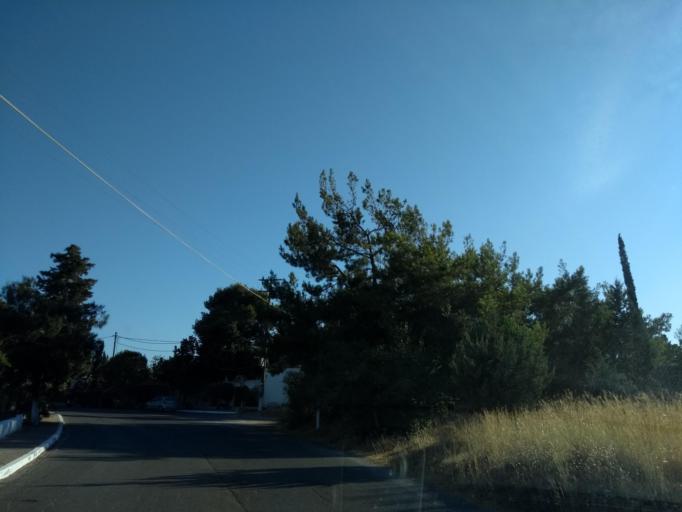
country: GR
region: Crete
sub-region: Nomos Chanias
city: Pithari
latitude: 35.5229
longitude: 24.0777
